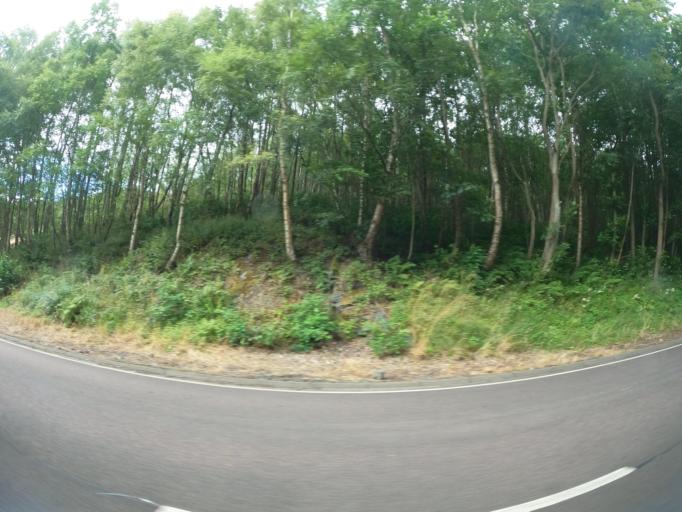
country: GB
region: Scotland
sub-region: Stirling
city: Callander
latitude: 56.3932
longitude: -4.1776
